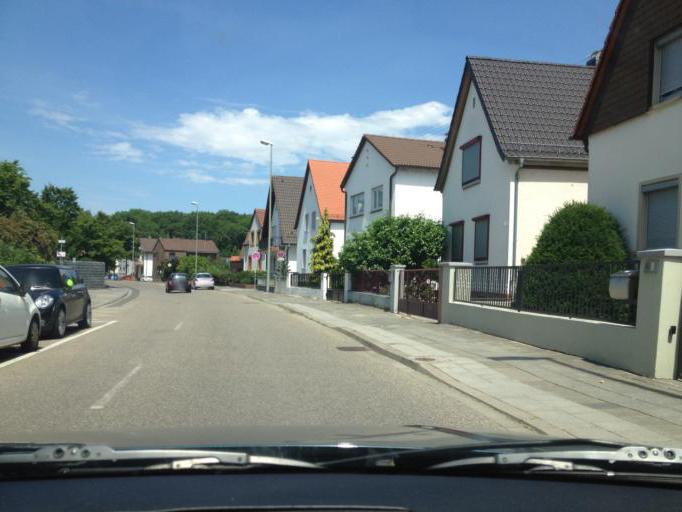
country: DE
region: Rheinland-Pfalz
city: Neuhofen
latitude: 49.4292
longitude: 8.4224
